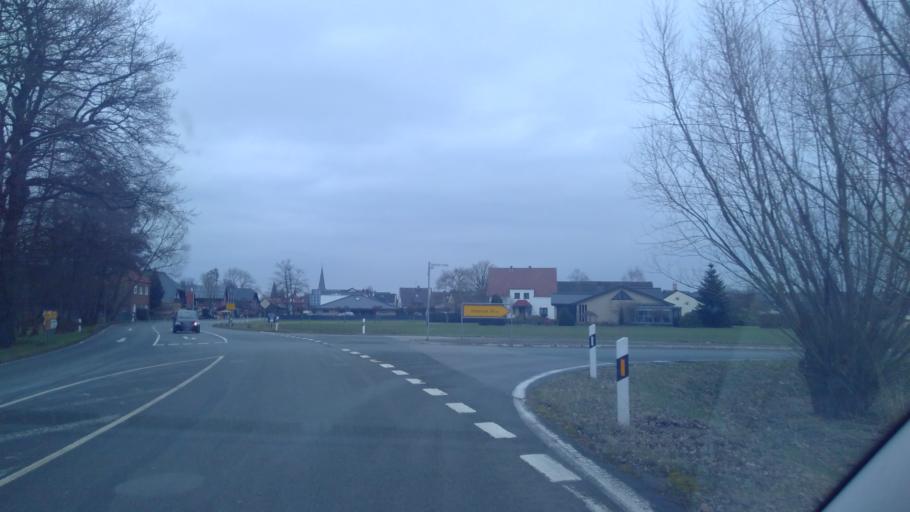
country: DE
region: North Rhine-Westphalia
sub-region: Regierungsbezirk Detmold
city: Verl
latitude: 51.8525
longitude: 8.5571
